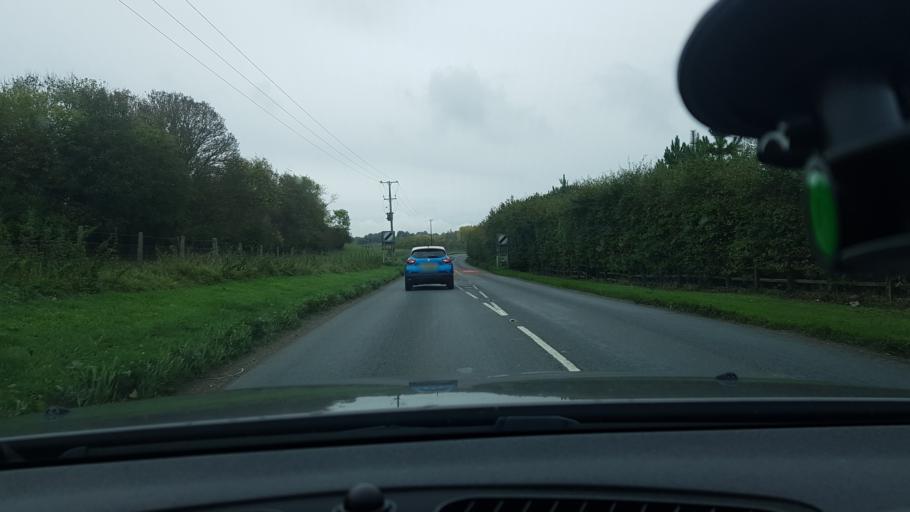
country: GB
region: England
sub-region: Wiltshire
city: Marlborough
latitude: 51.4432
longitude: -1.7311
